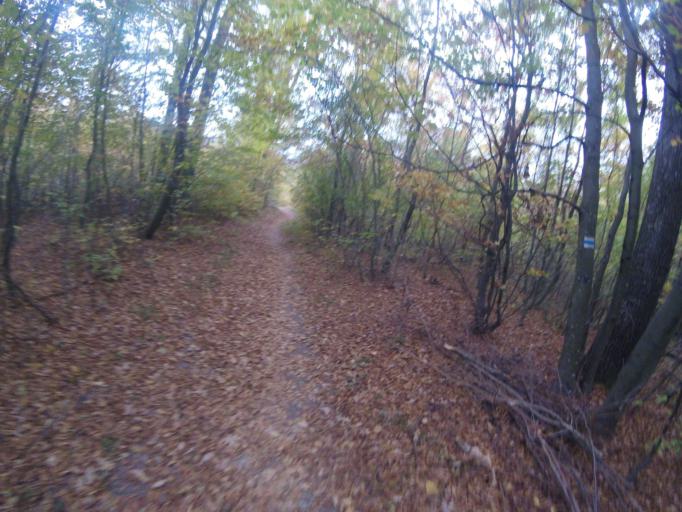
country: HU
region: Veszprem
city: Herend
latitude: 47.2624
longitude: 17.7429
